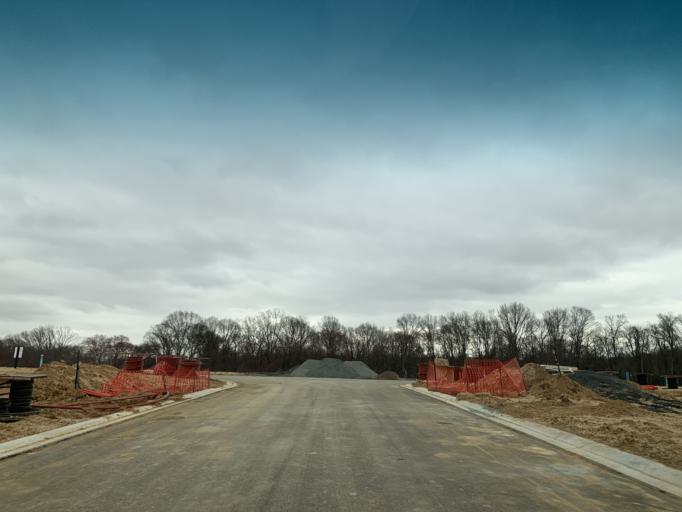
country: US
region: Maryland
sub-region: Harford County
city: Aberdeen
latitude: 39.5402
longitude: -76.1949
